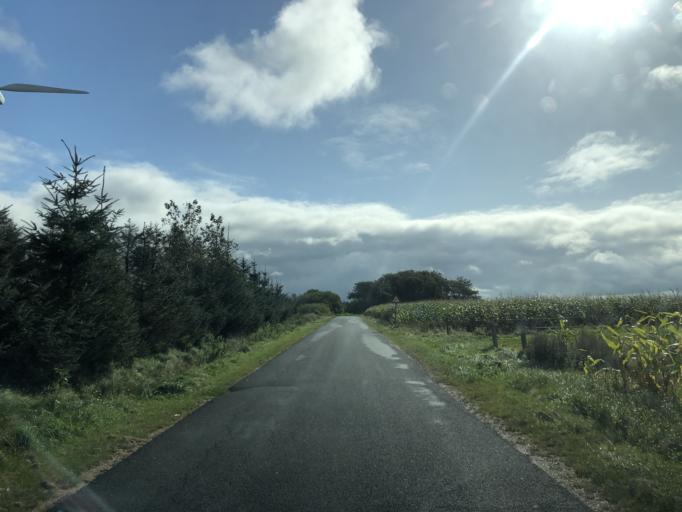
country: DK
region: Central Jutland
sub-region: Holstebro Kommune
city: Ulfborg
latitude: 56.3013
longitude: 8.4579
